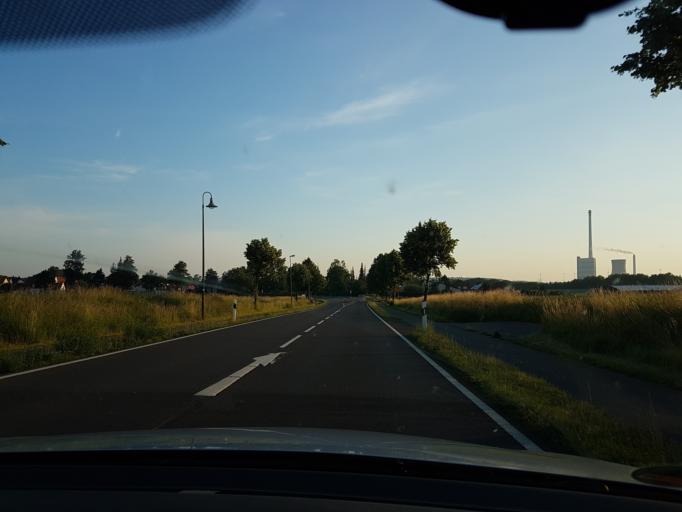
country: DE
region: Lower Saxony
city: Schoningen
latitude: 52.1526
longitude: 10.9660
